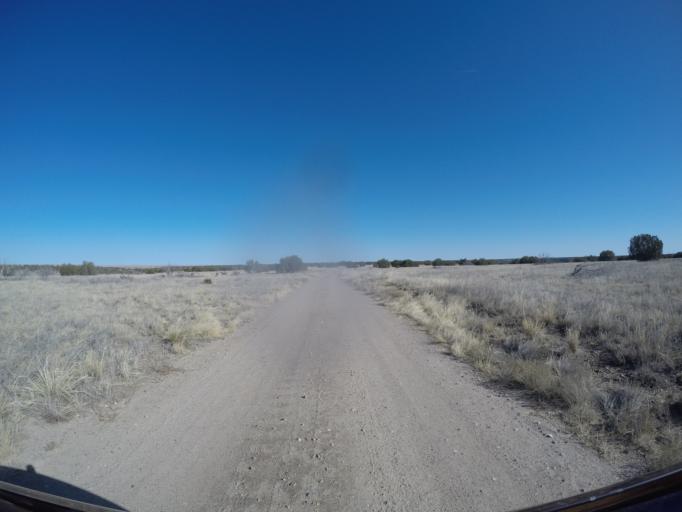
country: US
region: Colorado
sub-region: Otero County
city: La Junta
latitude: 37.6571
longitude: -103.5869
